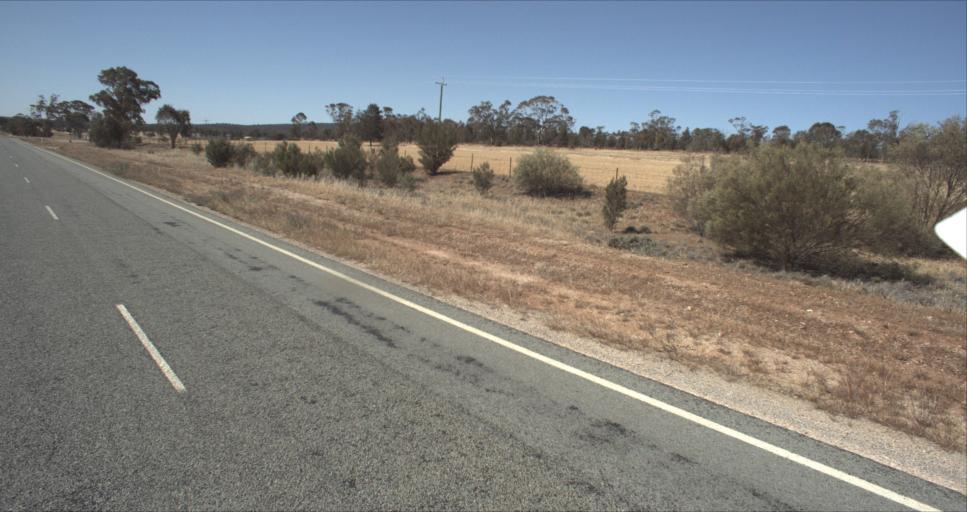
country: AU
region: New South Wales
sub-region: Leeton
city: Leeton
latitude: -34.4764
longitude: 146.4350
